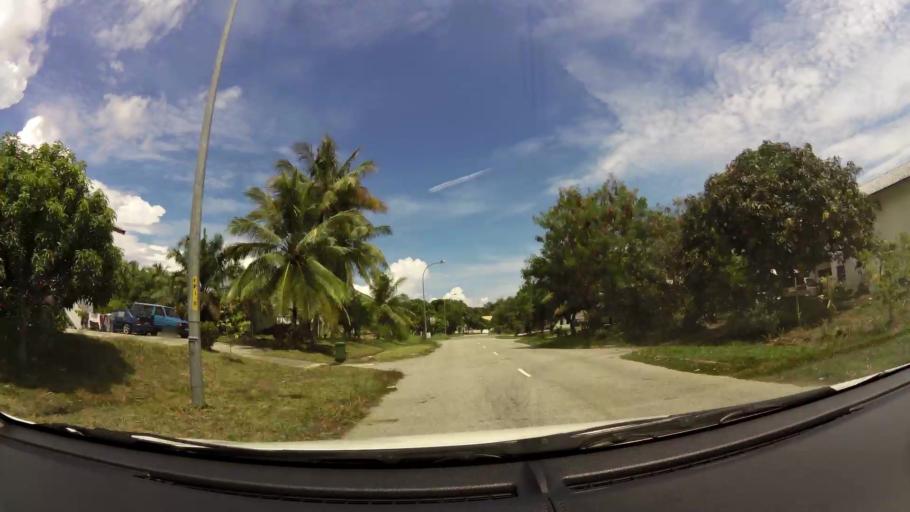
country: BN
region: Brunei and Muara
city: Bandar Seri Begawan
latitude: 4.9585
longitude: 114.9001
